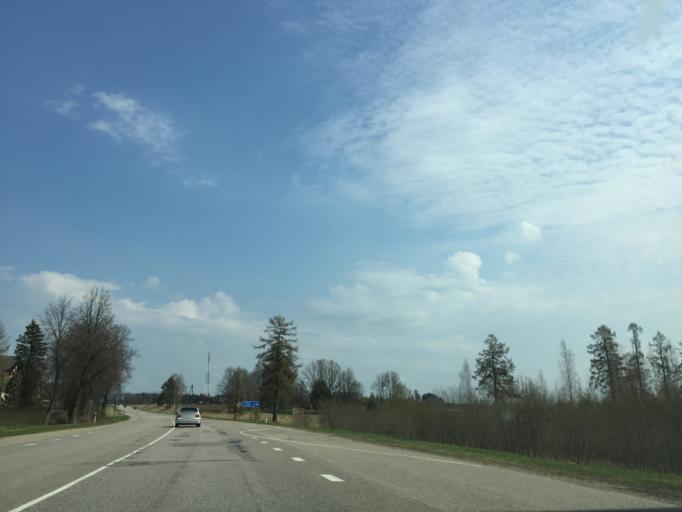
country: LV
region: Apes Novads
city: Ape
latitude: 57.4765
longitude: 26.5274
